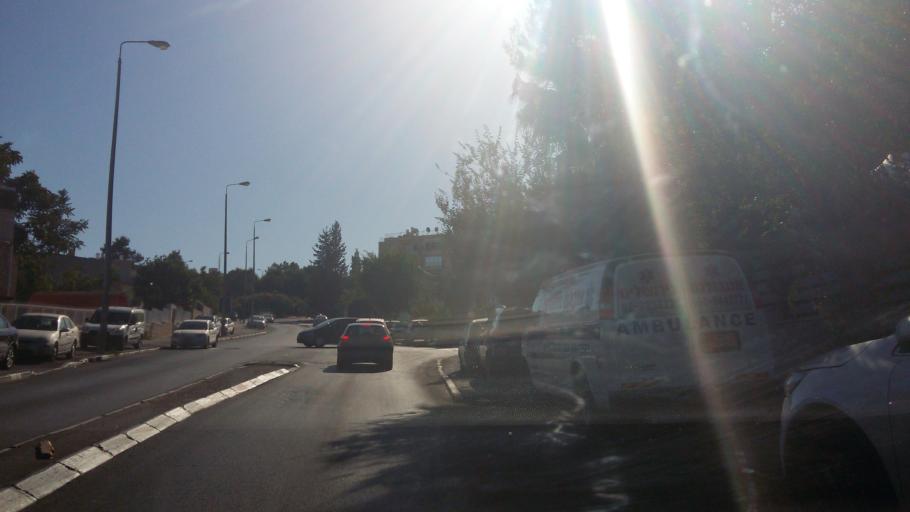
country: IL
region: Jerusalem
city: Jerusalem
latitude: 31.7593
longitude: 35.2103
